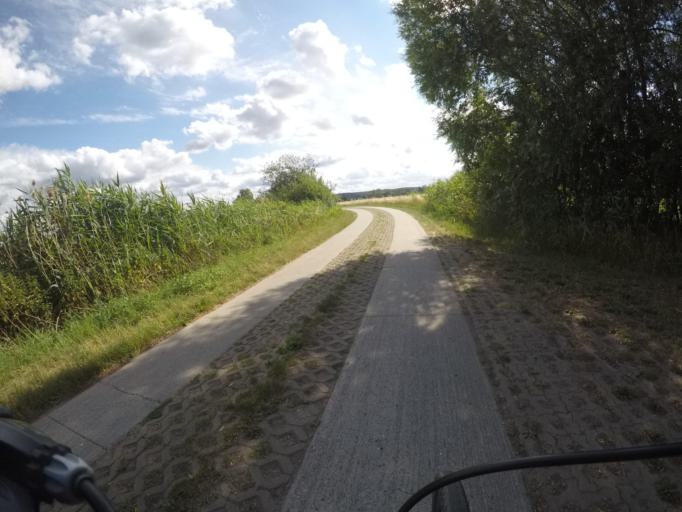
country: DE
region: Lower Saxony
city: Neu Darchau
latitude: 53.2405
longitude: 10.9308
